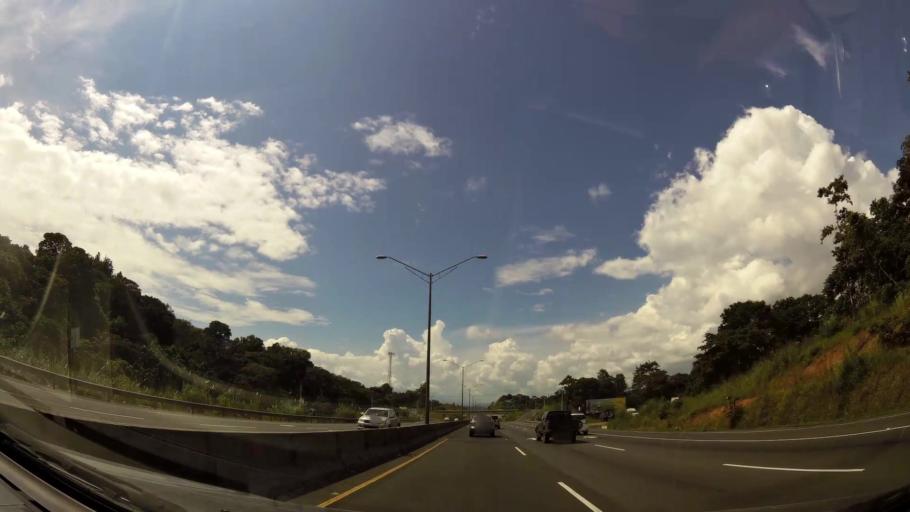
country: PA
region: Panama
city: San Vicente de Bique
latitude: 8.9332
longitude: -79.6829
